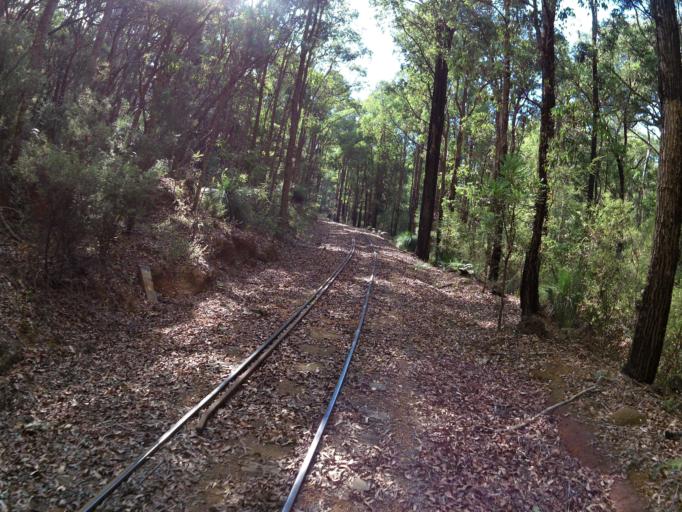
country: AU
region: Western Australia
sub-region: Waroona
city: Waroona
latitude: -32.7338
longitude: 116.1148
